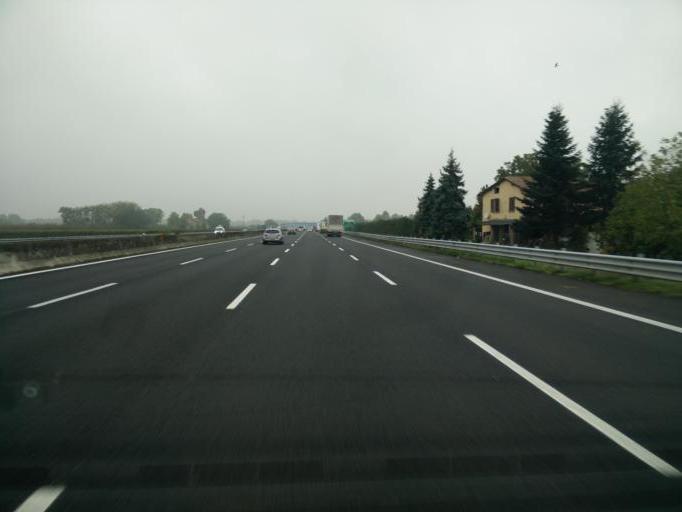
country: IT
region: Emilia-Romagna
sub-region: Provincia di Modena
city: San Cesario sul Panaro
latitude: 44.5723
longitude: 11.0087
